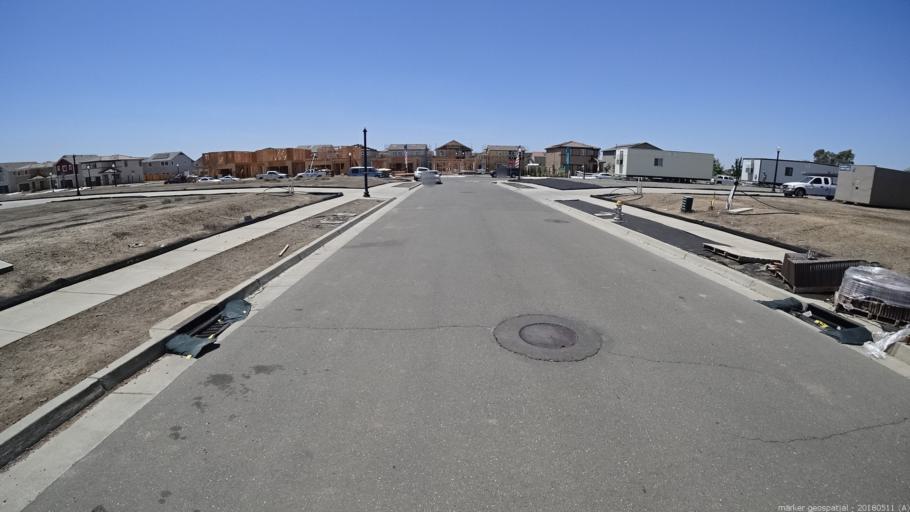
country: US
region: California
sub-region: Yolo County
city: West Sacramento
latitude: 38.6520
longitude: -121.5456
